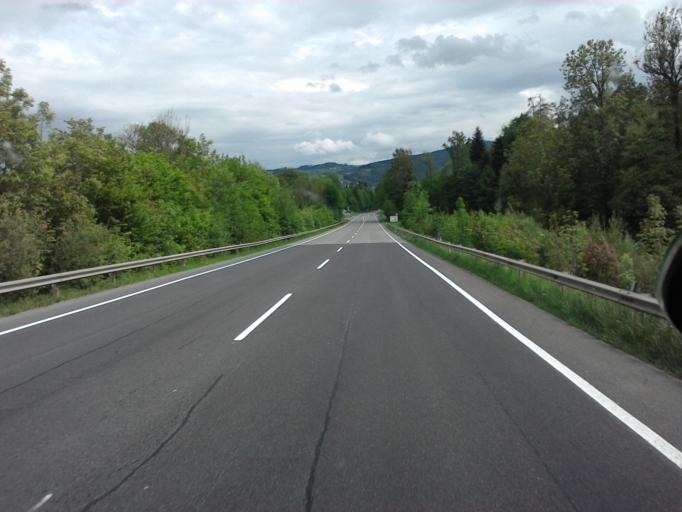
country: AT
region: Upper Austria
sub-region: Politischer Bezirk Kirchdorf an der Krems
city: Micheldorf in Oberoesterreich
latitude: 47.9536
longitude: 14.0886
